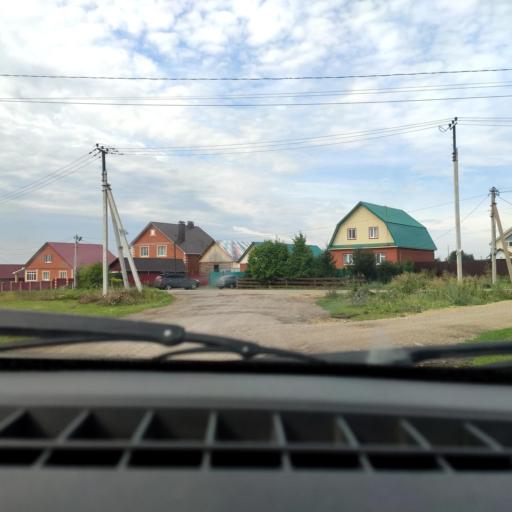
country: RU
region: Bashkortostan
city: Avdon
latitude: 54.6577
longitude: 55.7767
